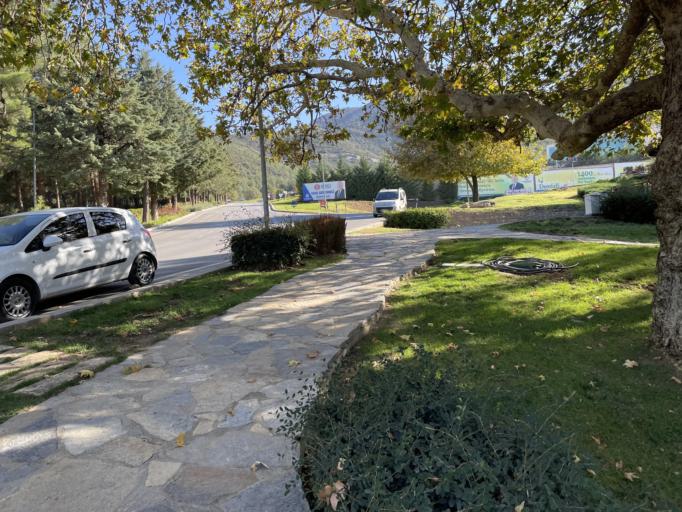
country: TR
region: Denizli
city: Denizli
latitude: 37.7230
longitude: 29.1401
